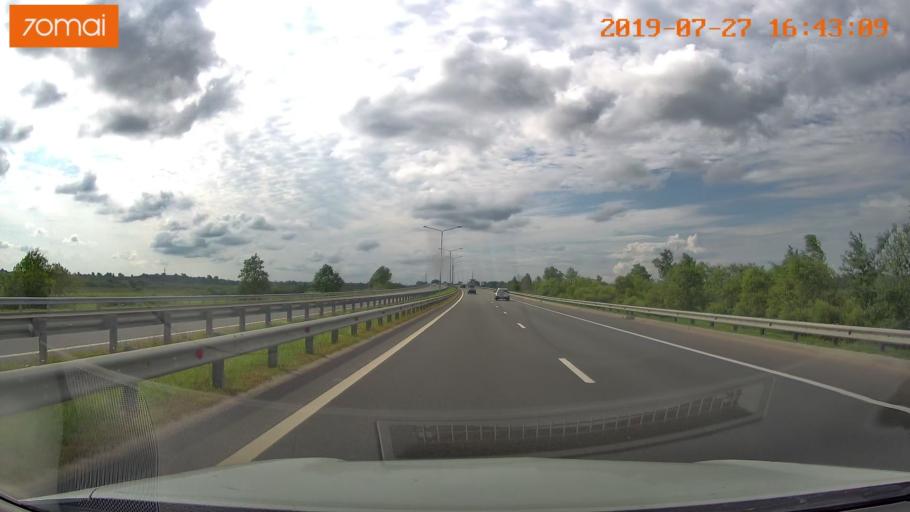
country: RU
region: Kaliningrad
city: Gvardeysk
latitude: 54.6696
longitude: 21.1098
